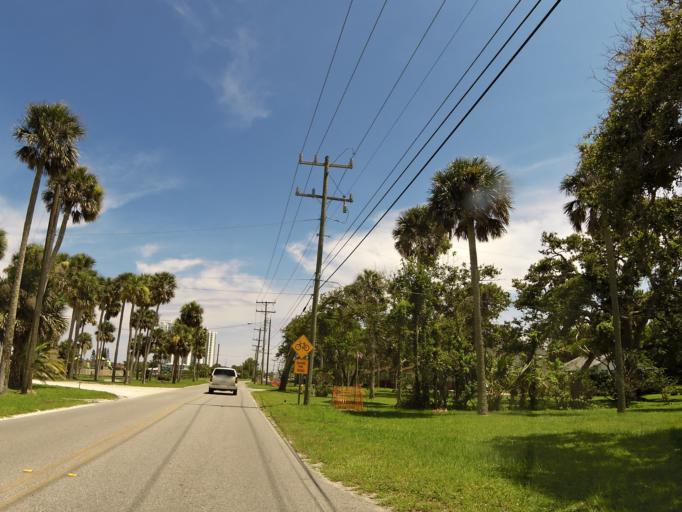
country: US
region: Florida
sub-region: Volusia County
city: Holly Hill
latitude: 29.2386
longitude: -81.0327
